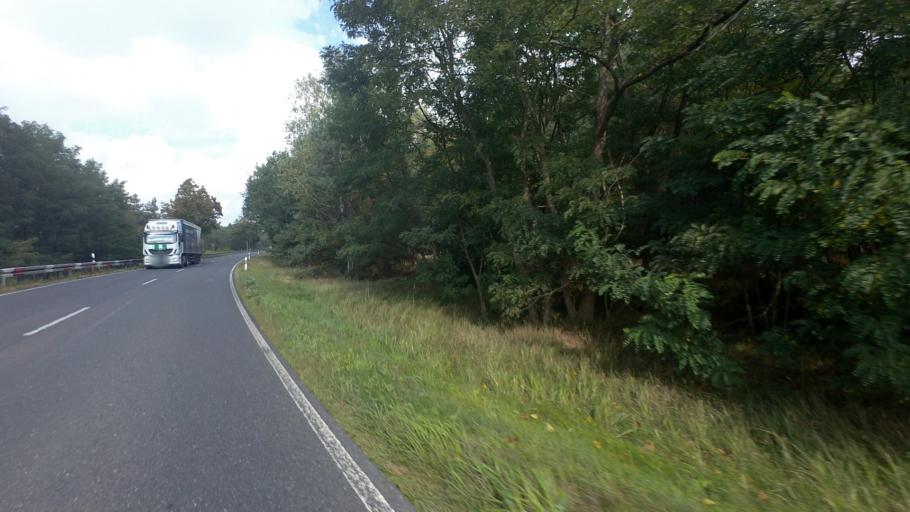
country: DE
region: Saxony-Anhalt
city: Holzdorf
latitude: 51.7690
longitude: 13.1987
